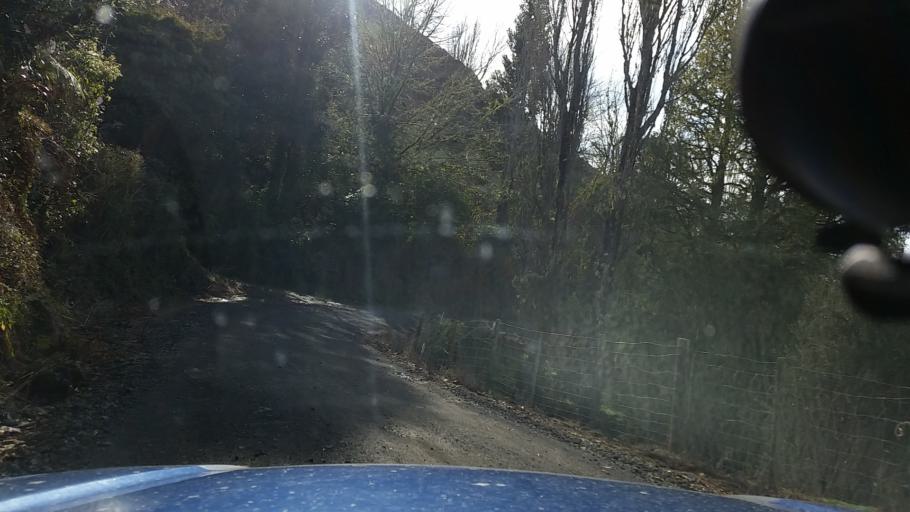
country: NZ
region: Taranaki
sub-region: New Plymouth District
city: Waitara
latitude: -39.0338
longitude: 174.7845
